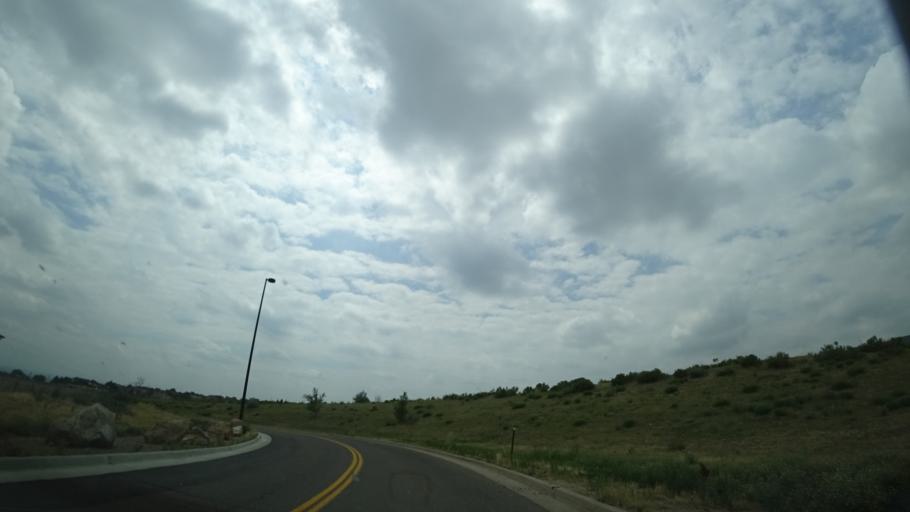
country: US
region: Colorado
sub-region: Jefferson County
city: West Pleasant View
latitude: 39.7124
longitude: -105.1525
